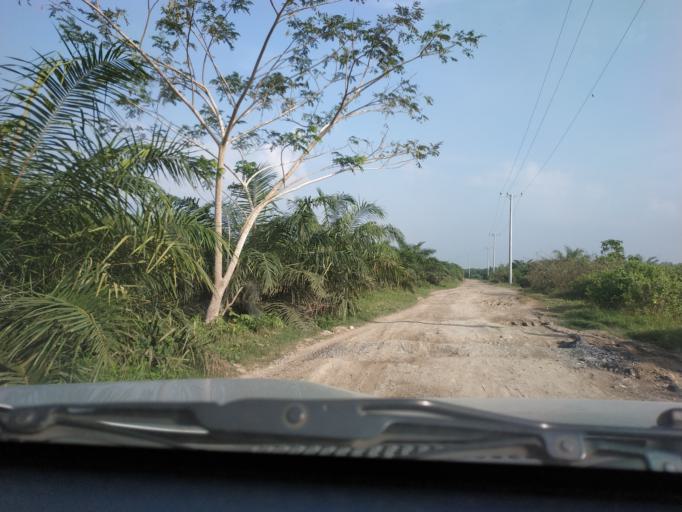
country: ID
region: North Sumatra
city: Teluk Nibung
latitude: 3.0830
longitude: 99.7904
